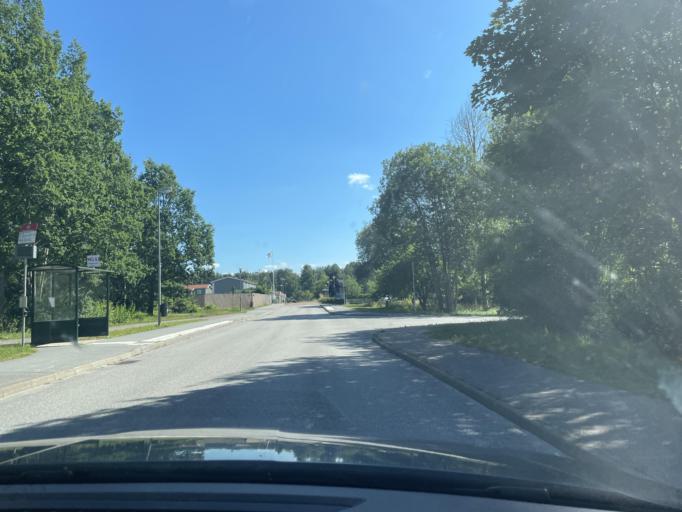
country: SE
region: Stockholm
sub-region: Sigtuna Kommun
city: Rosersberg
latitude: 59.5839
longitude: 17.8818
